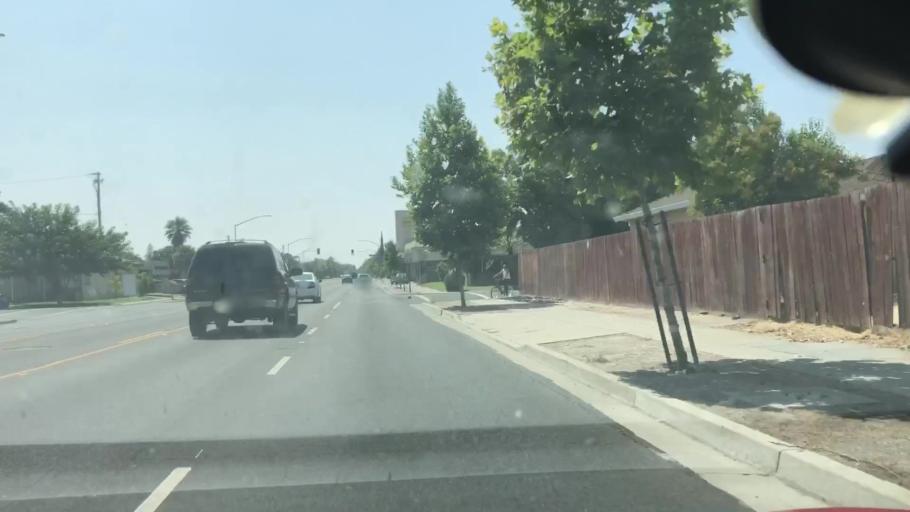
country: US
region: California
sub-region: San Joaquin County
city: Lincoln Village
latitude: 37.9875
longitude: -121.3025
